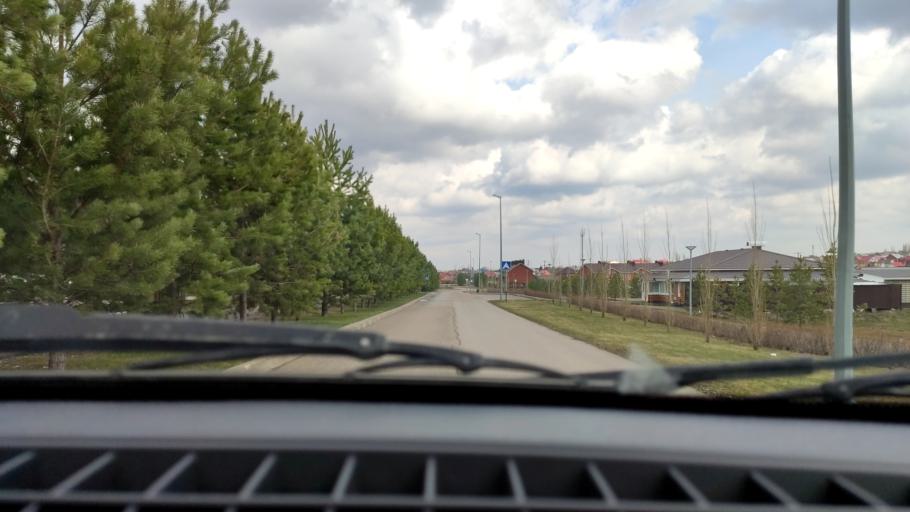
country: RU
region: Bashkortostan
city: Ufa
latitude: 54.5957
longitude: 55.9234
